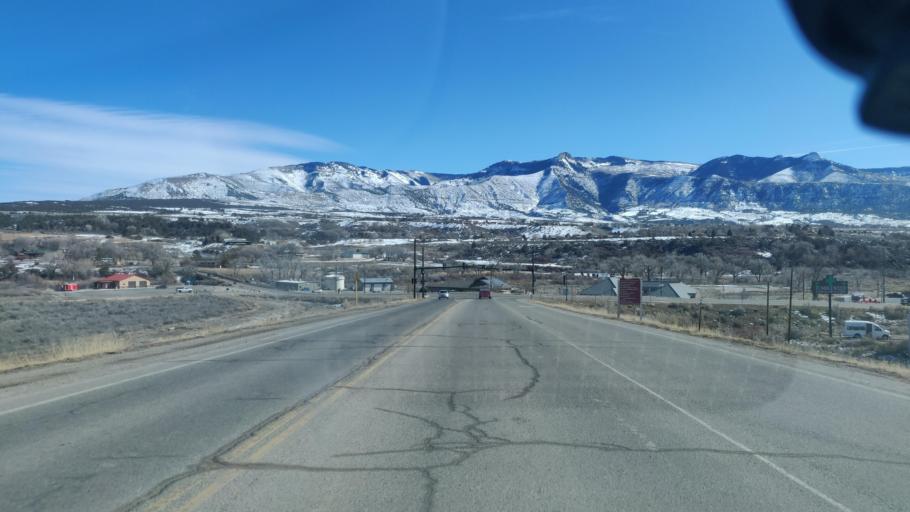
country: US
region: Colorado
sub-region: Garfield County
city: Parachute
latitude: 39.4546
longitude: -108.0458
